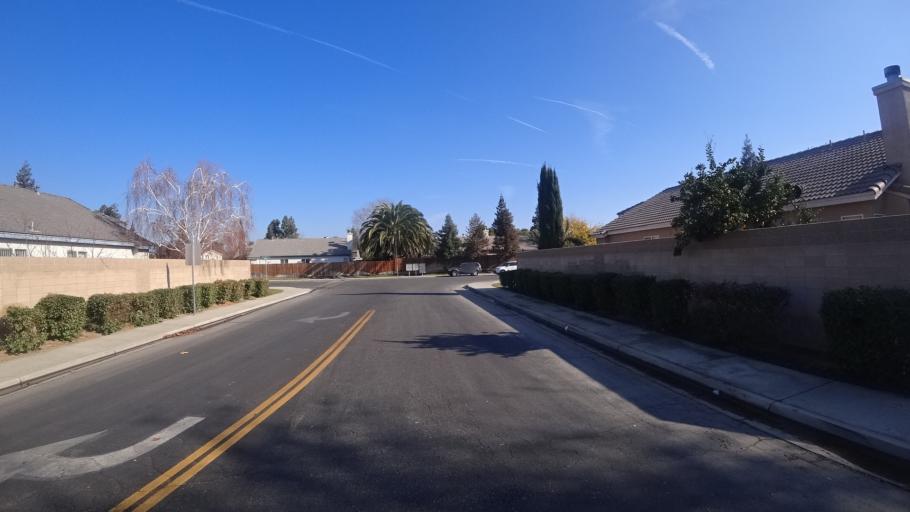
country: US
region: California
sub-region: Kern County
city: Greenacres
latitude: 35.3165
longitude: -119.1092
